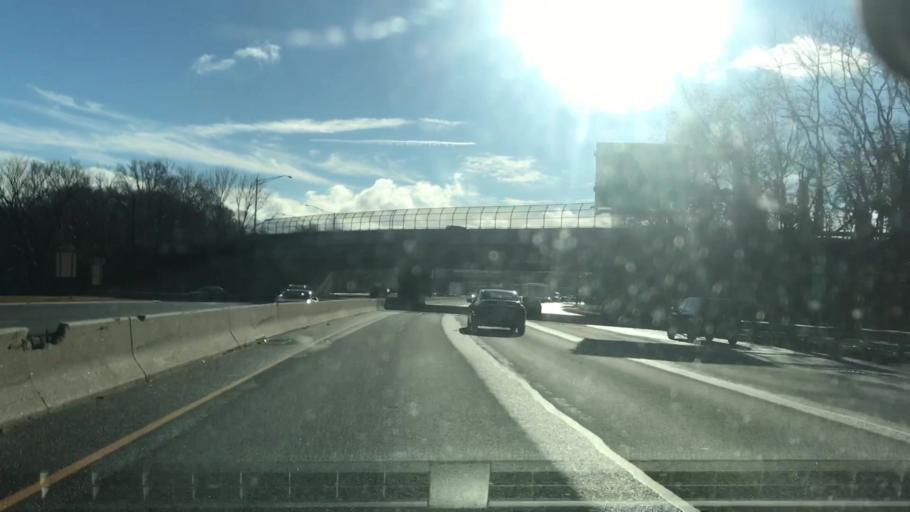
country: US
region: New Jersey
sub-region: Bergen County
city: Ho-Ho-Kus
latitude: 40.9808
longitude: -74.0851
